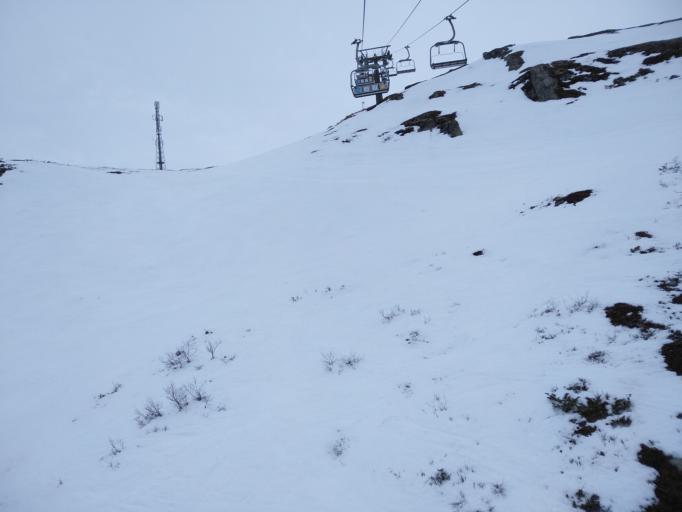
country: NO
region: Aust-Agder
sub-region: Bykle
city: Hovden
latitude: 59.5776
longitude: 7.3354
